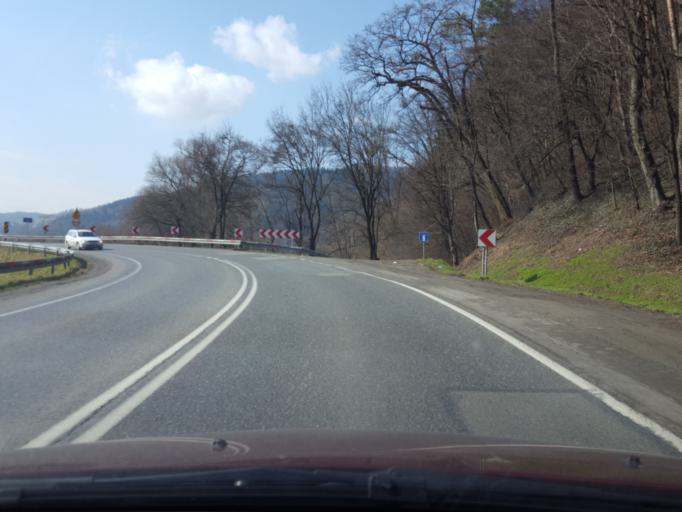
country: PL
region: Lesser Poland Voivodeship
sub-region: Powiat nowosadecki
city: Lososina Dolna
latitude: 49.6925
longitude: 20.6549
